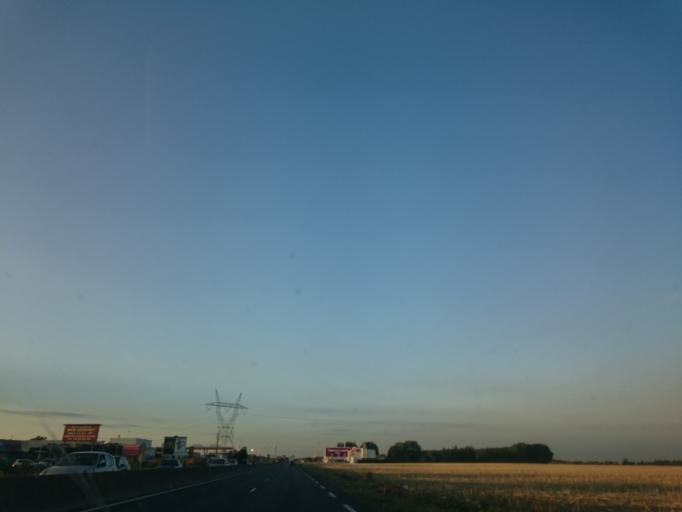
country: FR
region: Ile-de-France
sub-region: Departement de l'Essonne
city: Egly
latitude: 48.5665
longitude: 2.2308
